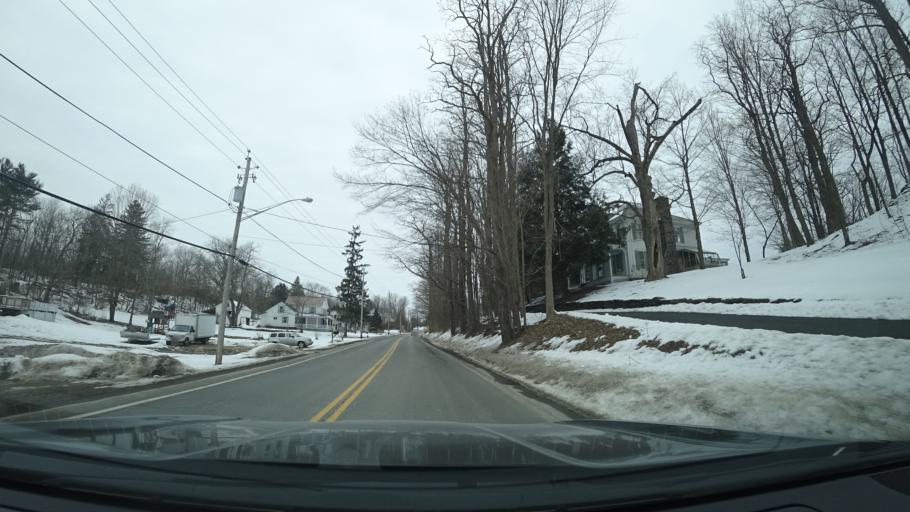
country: US
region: New York
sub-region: Washington County
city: Cambridge
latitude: 43.1785
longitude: -73.3268
